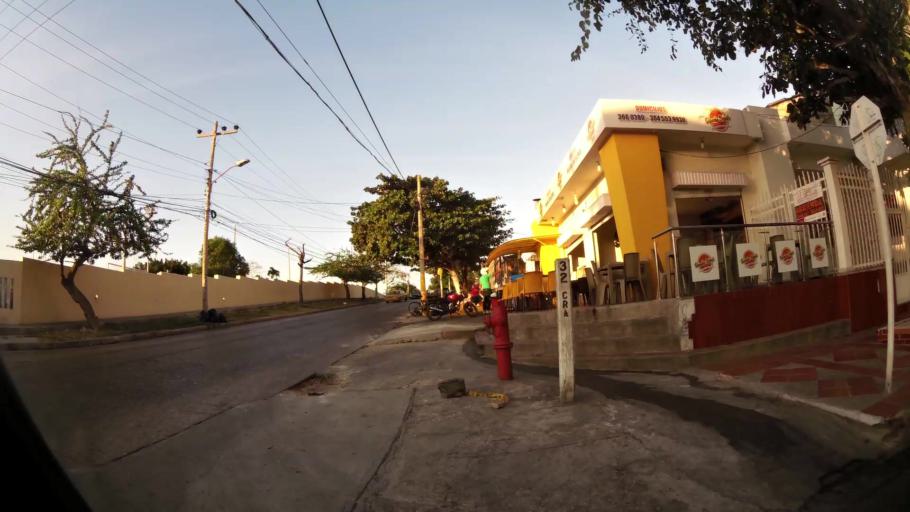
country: CO
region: Atlantico
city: Barranquilla
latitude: 10.9794
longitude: -74.8013
